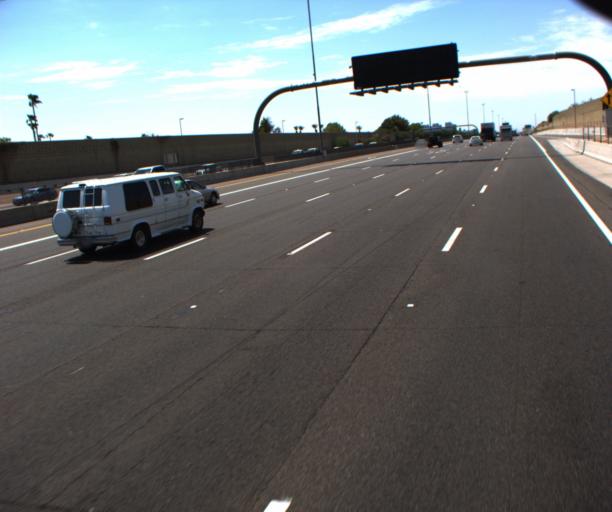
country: US
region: Arizona
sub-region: Maricopa County
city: Tempe
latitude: 33.3859
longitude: -111.9117
